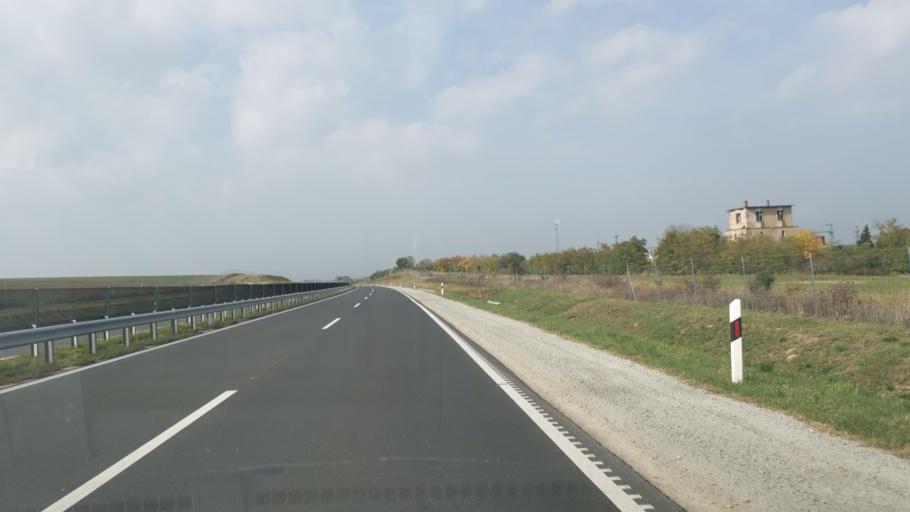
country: HU
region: Gyor-Moson-Sopron
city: Nagycenk
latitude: 47.5994
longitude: 16.6926
